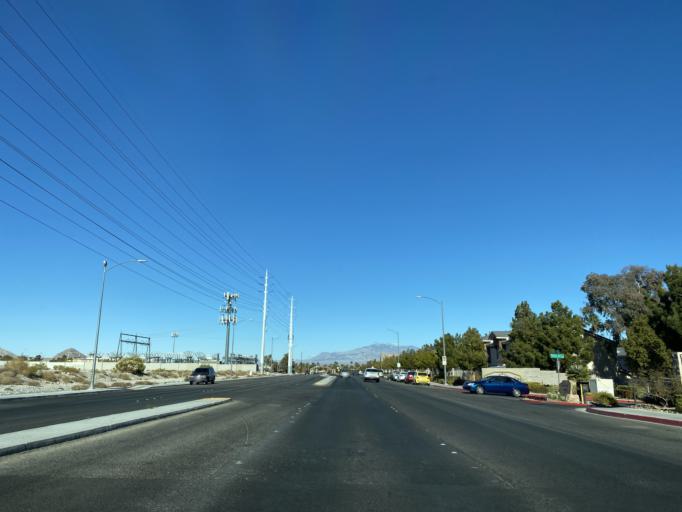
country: US
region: Nevada
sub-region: Clark County
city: Spring Valley
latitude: 36.1845
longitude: -115.2784
